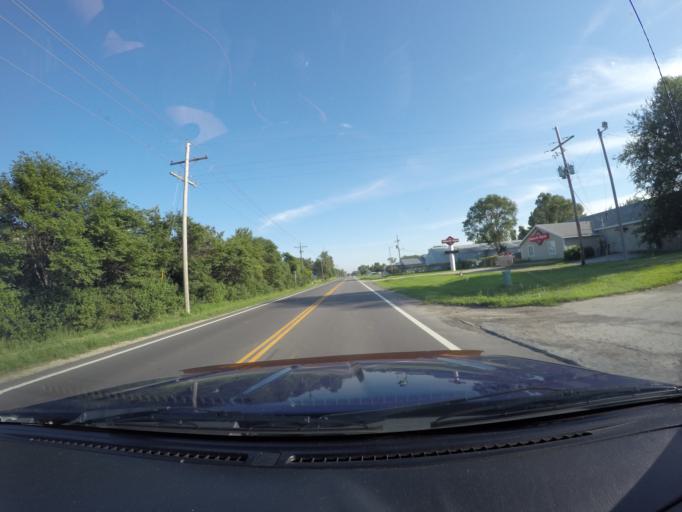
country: US
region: Kansas
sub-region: Douglas County
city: Lawrence
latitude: 39.0067
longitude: -95.2335
